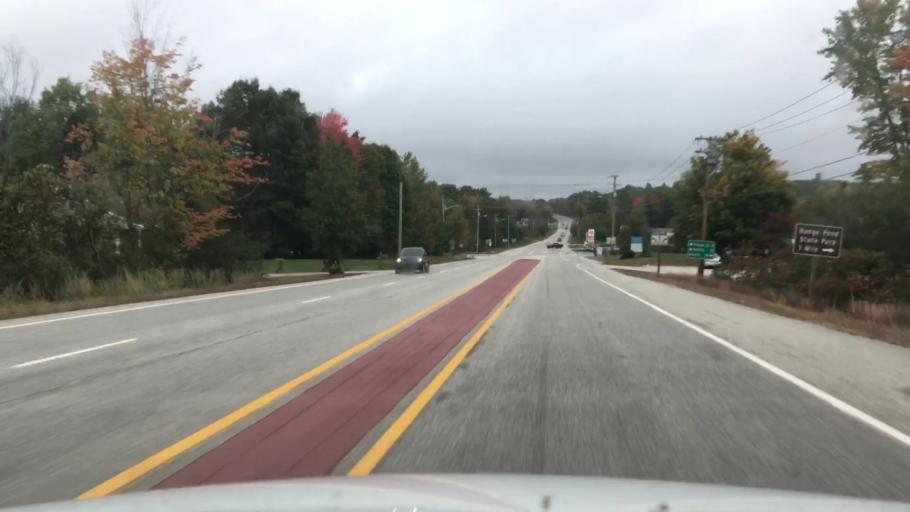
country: US
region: Maine
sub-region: Androscoggin County
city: Poland
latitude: 44.0118
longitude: -70.3625
